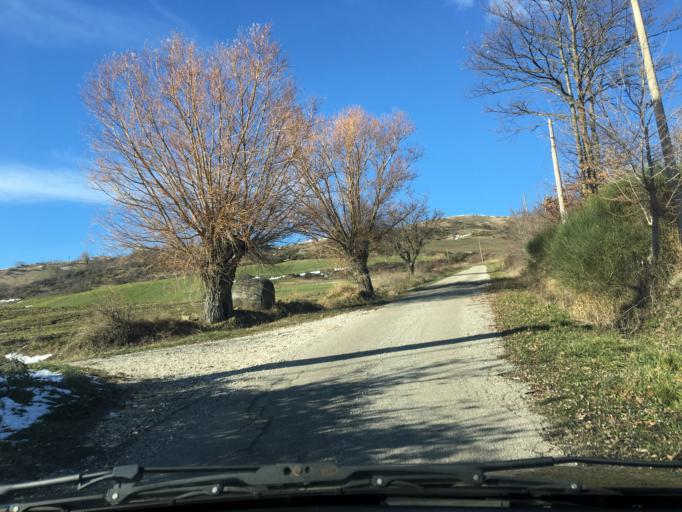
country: IT
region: Molise
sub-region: Provincia di Isernia
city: Agnone
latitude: 41.8460
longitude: 14.3534
